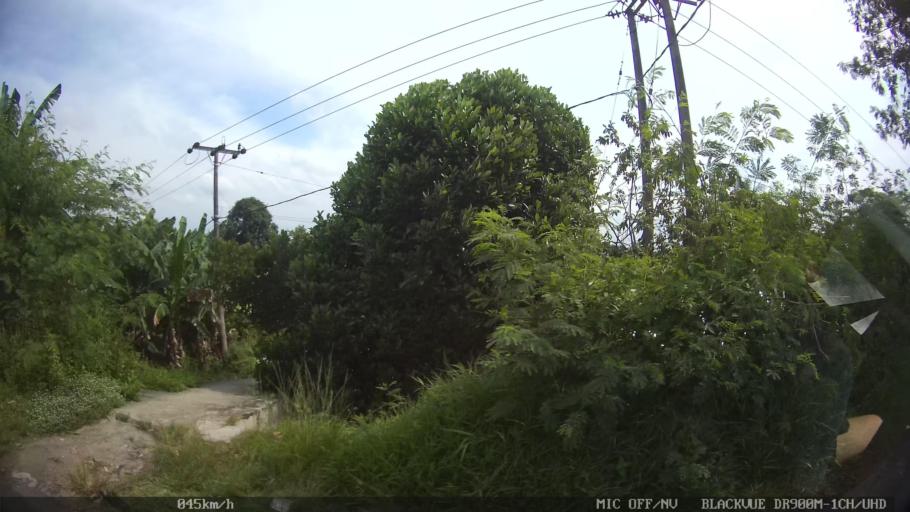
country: ID
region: North Sumatra
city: Percut
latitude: 3.6162
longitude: 98.8352
